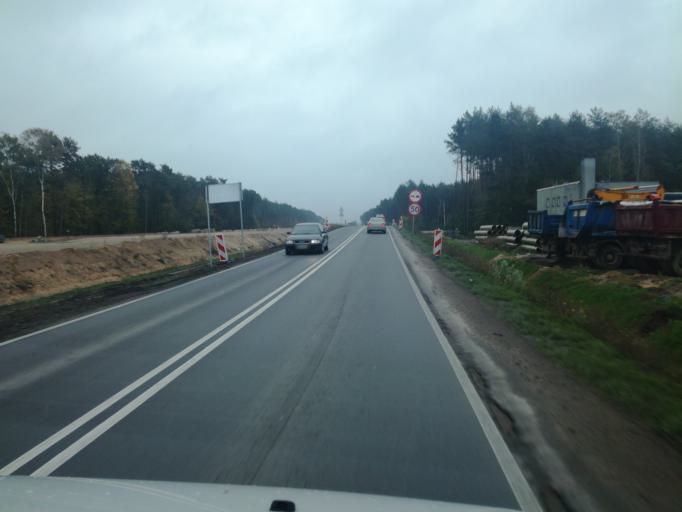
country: PL
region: Masovian Voivodeship
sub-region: Powiat wyszkowski
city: Branszczyk
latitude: 52.6682
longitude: 21.5982
